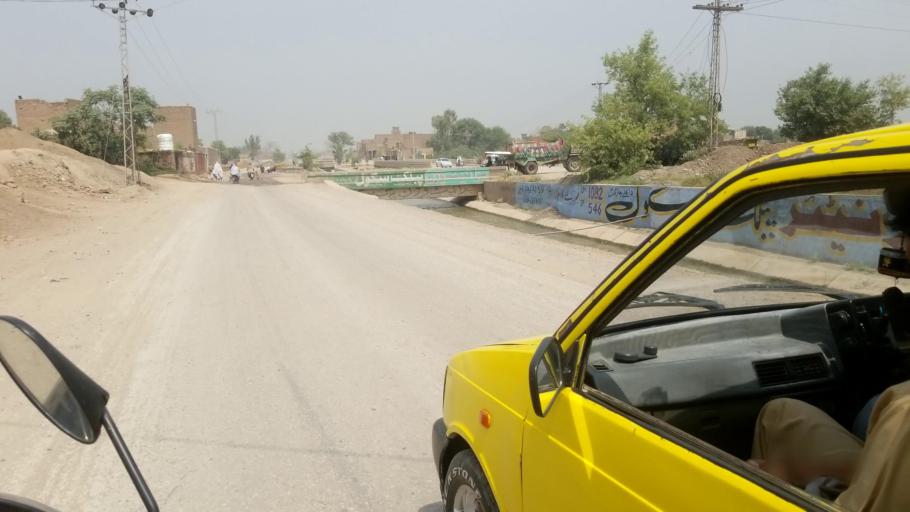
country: PK
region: Khyber Pakhtunkhwa
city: Peshawar
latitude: 33.9619
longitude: 71.5424
